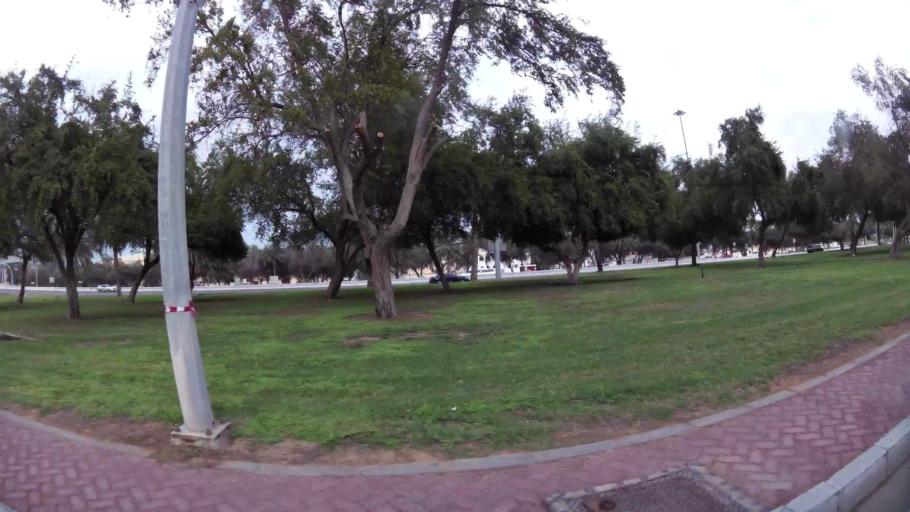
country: AE
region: Abu Dhabi
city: Abu Dhabi
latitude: 24.4439
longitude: 54.3945
